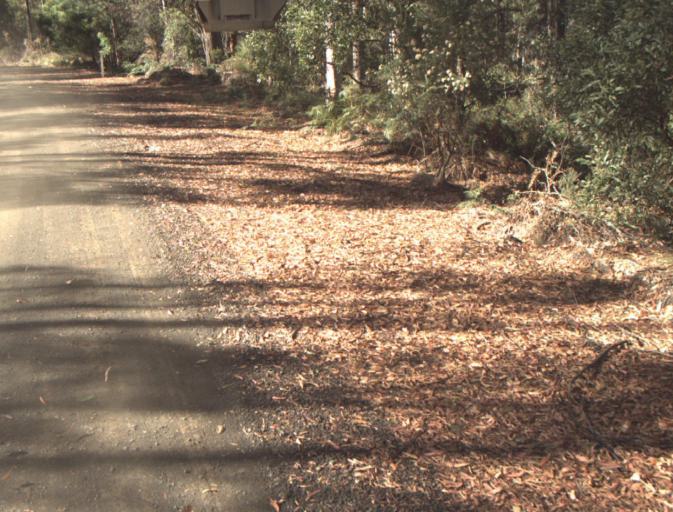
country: AU
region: Tasmania
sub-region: Launceston
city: Newstead
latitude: -41.3037
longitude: 147.3331
